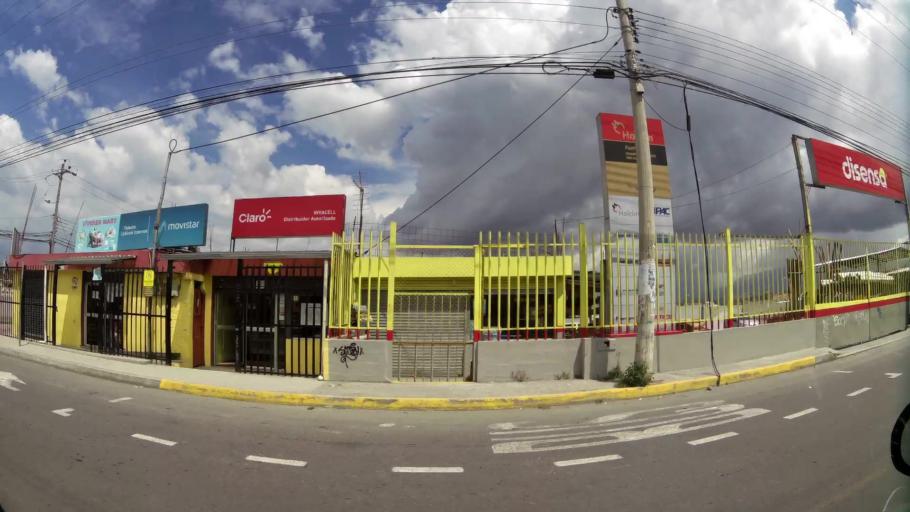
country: EC
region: Pichincha
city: Quito
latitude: -0.0642
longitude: -78.4146
